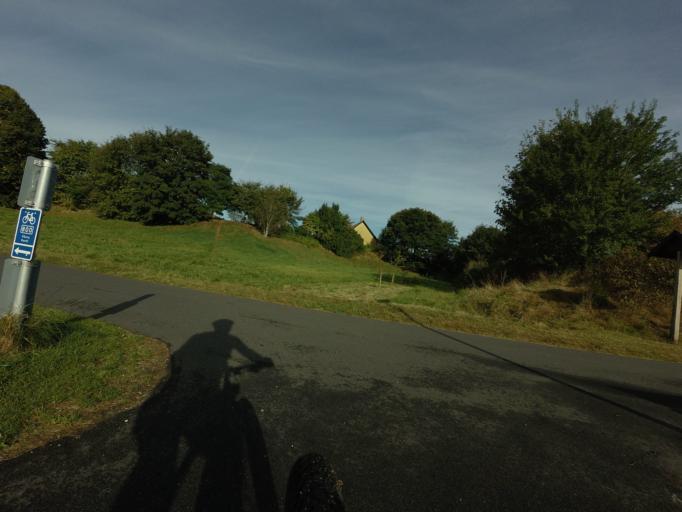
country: DK
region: Central Jutland
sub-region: Viborg Kommune
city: Viborg
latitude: 56.4300
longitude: 9.3957
